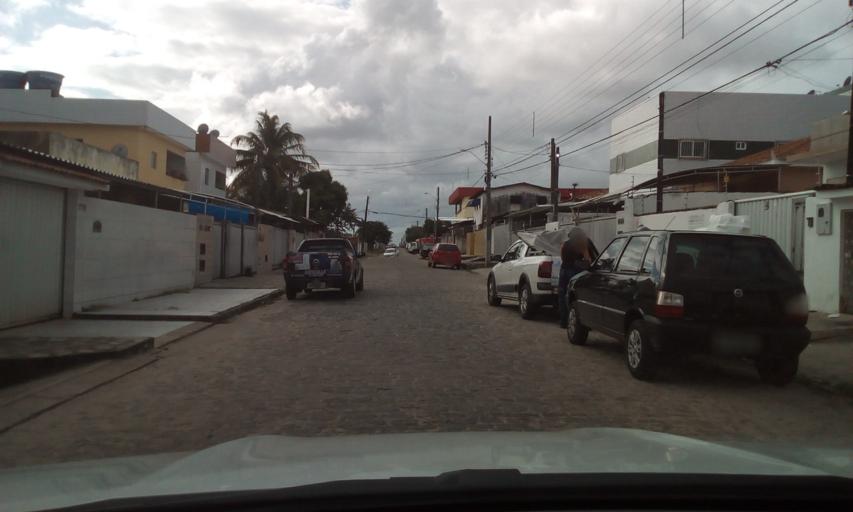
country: BR
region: Paraiba
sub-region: Joao Pessoa
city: Joao Pessoa
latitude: -7.1556
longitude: -34.8789
